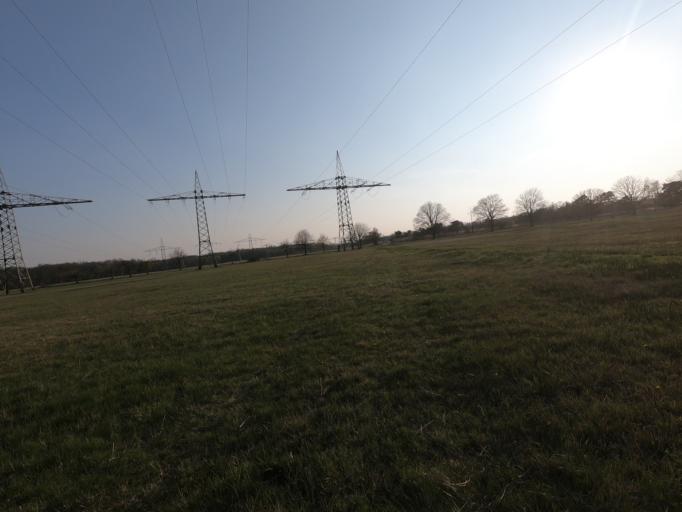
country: DE
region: Hesse
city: Morfelden-Walldorf
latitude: 49.9923
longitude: 8.5333
